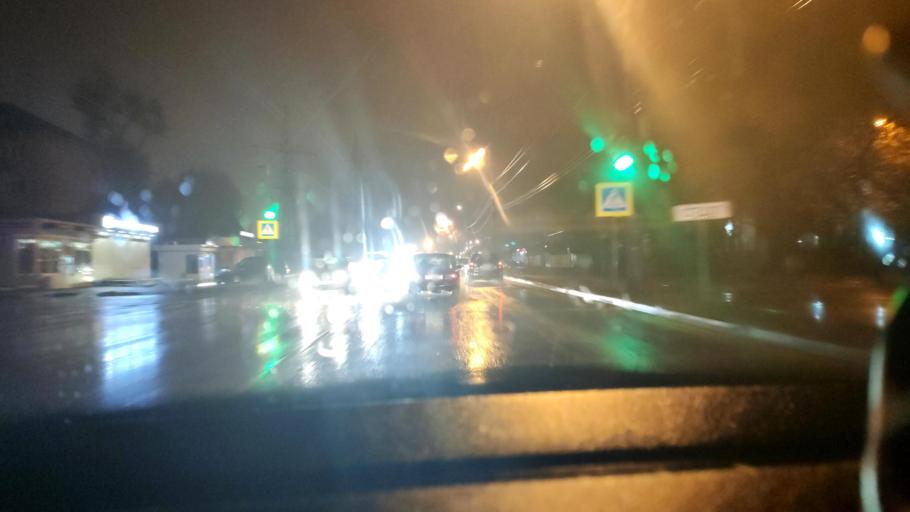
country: RU
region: Voronezj
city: Voronezh
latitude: 51.6412
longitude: 39.1582
